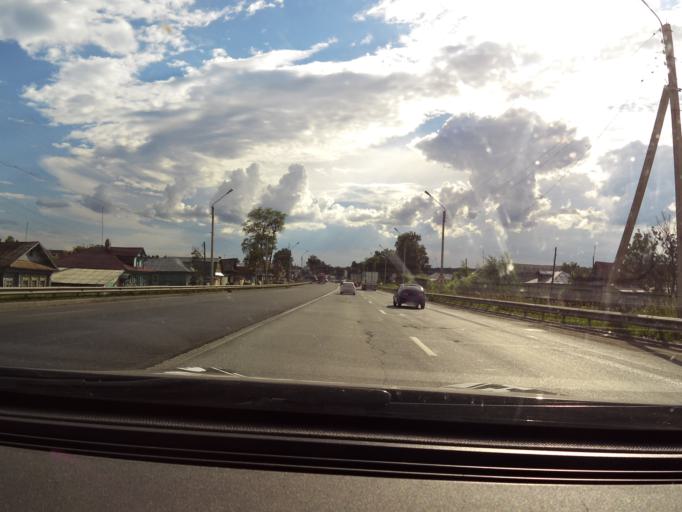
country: RU
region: Vladimir
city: Gorokhovets
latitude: 56.1993
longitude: 42.7053
